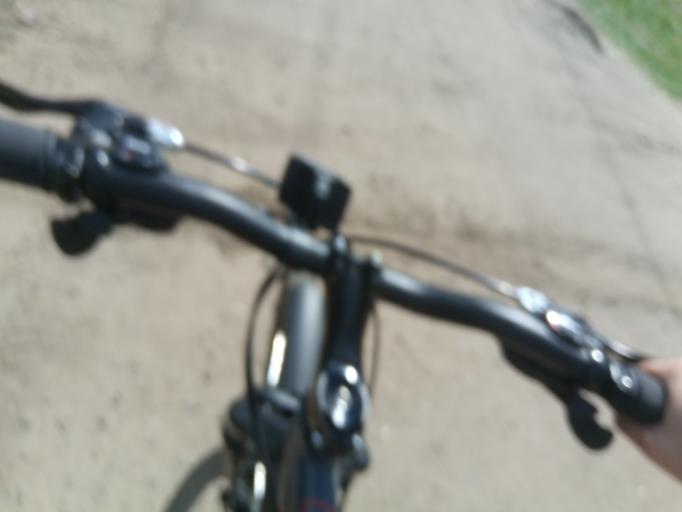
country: RU
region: Jaroslavl
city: Yaroslavl
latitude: 57.6582
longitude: 39.9645
